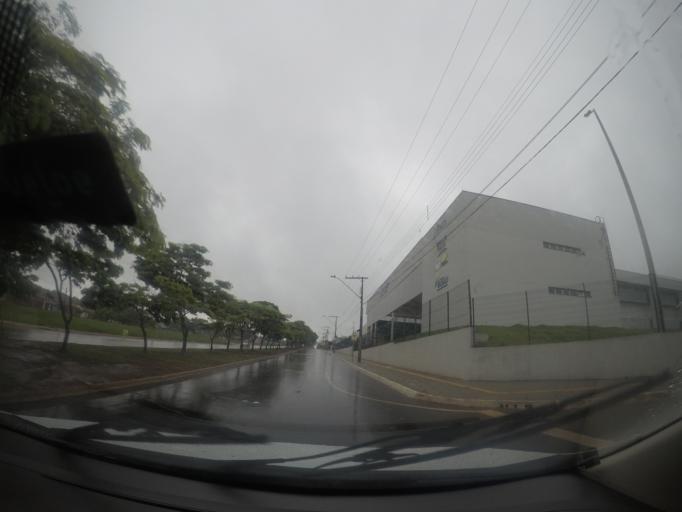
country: BR
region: Goias
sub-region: Goiania
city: Goiania
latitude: -16.5915
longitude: -49.3350
